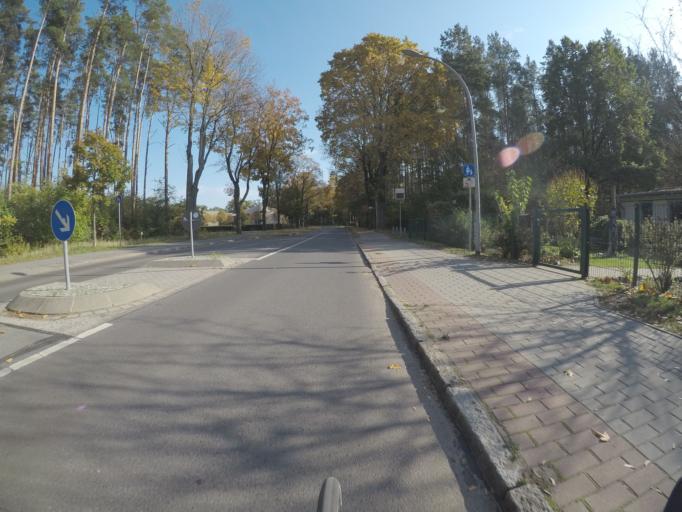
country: DE
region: Brandenburg
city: Hohen Neuendorf
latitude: 52.6772
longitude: 13.2575
